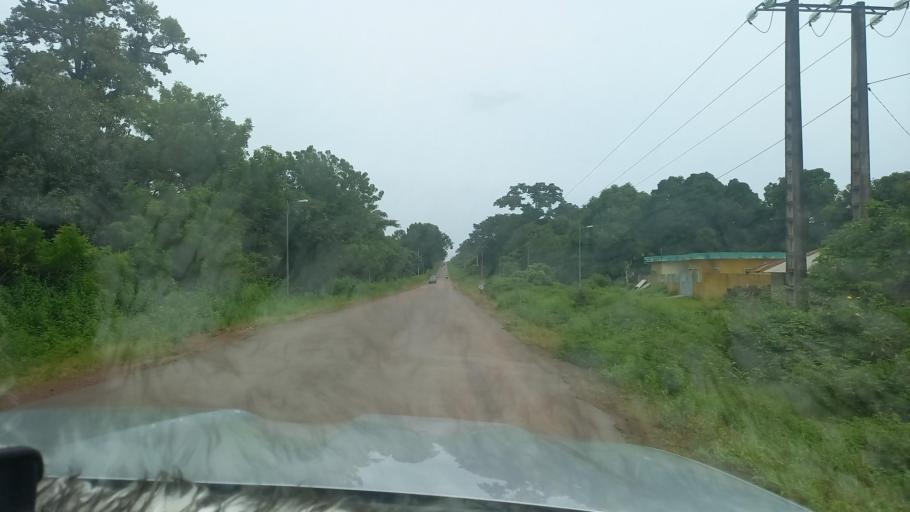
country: SN
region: Ziguinchor
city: Bignona
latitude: 12.8230
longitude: -16.1759
